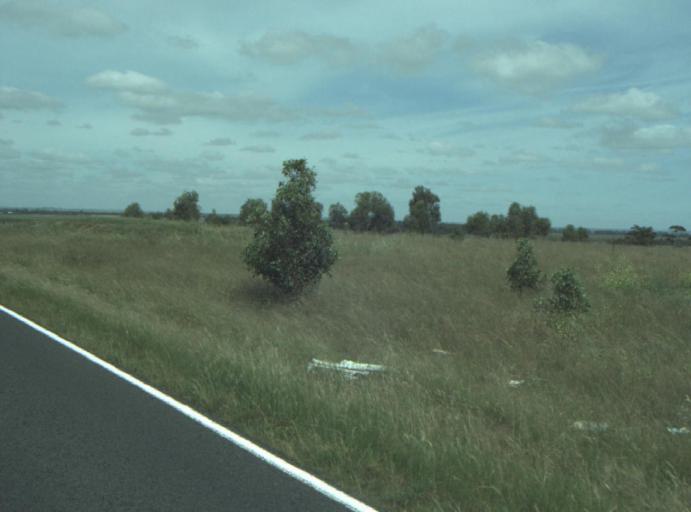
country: AU
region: Victoria
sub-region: Wyndham
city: Little River
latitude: -37.9973
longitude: 144.4785
